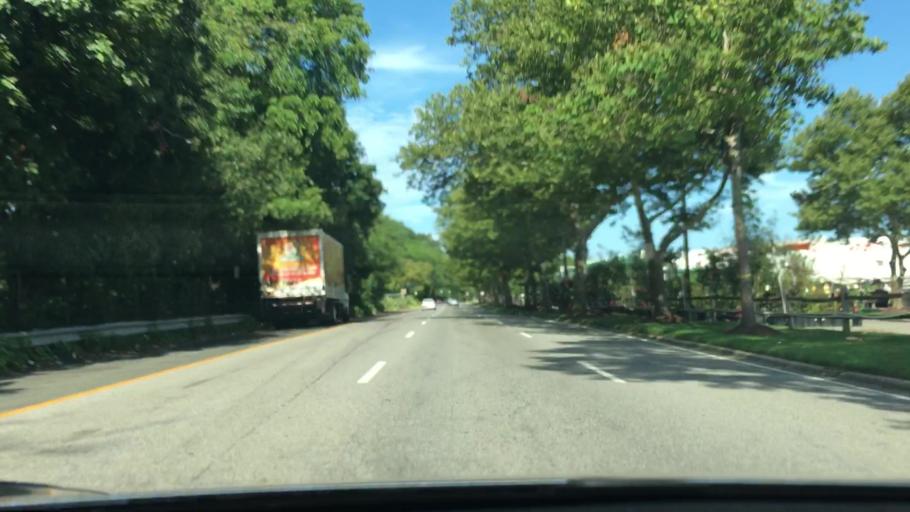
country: US
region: New York
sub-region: Nassau County
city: New Cassel
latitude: 40.7808
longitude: -73.5635
